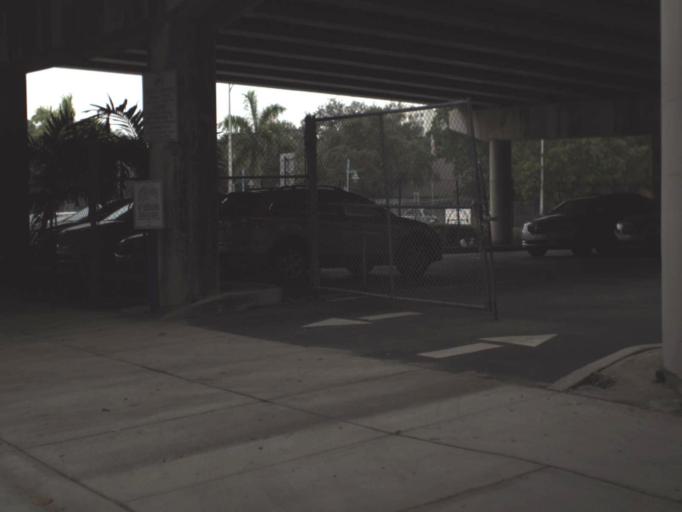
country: US
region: Florida
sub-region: Miami-Dade County
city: Miami
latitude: 25.7759
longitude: -80.1997
